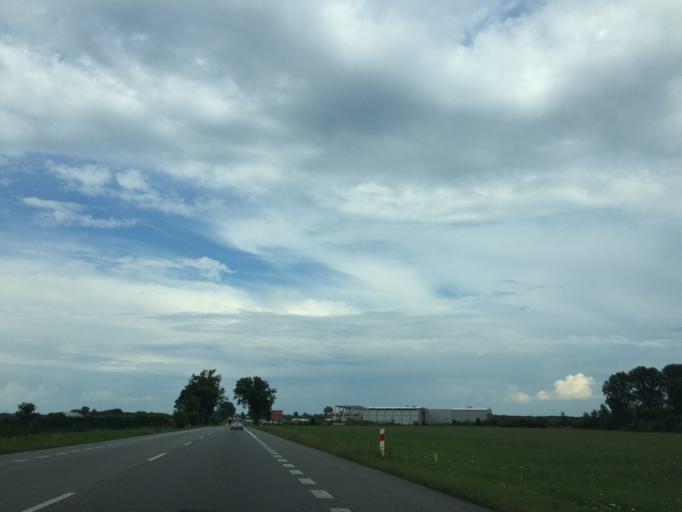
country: PL
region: Masovian Voivodeship
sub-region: Powiat piaseczynski
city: Prazmow
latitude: 51.8905
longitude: 20.9733
